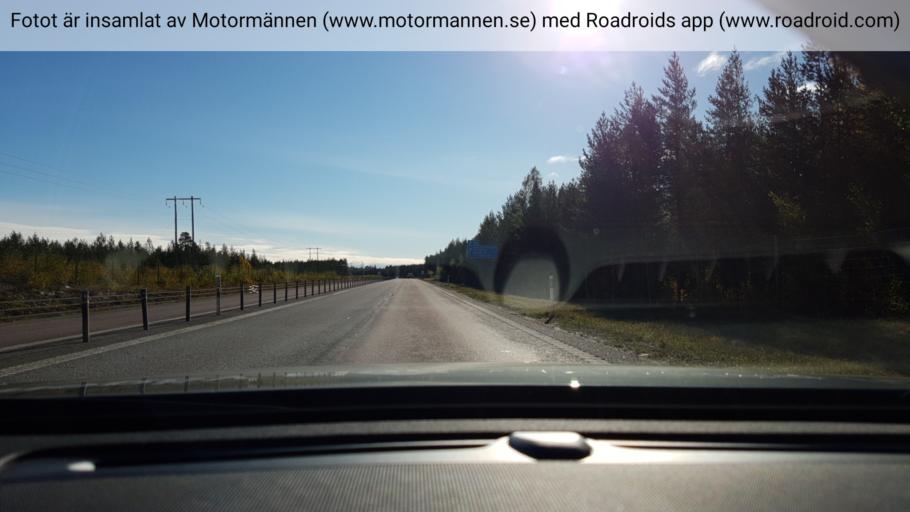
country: SE
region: Vaesterbotten
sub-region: Skelleftea Kommun
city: Soedra Bergsbyn
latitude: 64.6533
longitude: 21.1257
